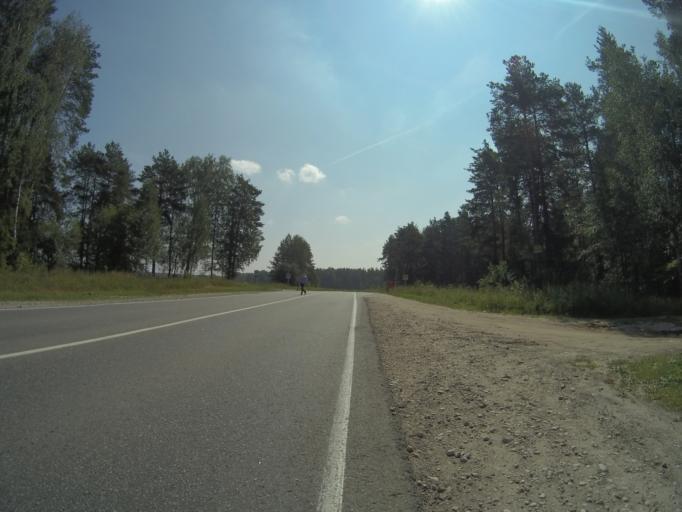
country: RU
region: Vladimir
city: Anopino
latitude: 55.7053
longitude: 40.7388
